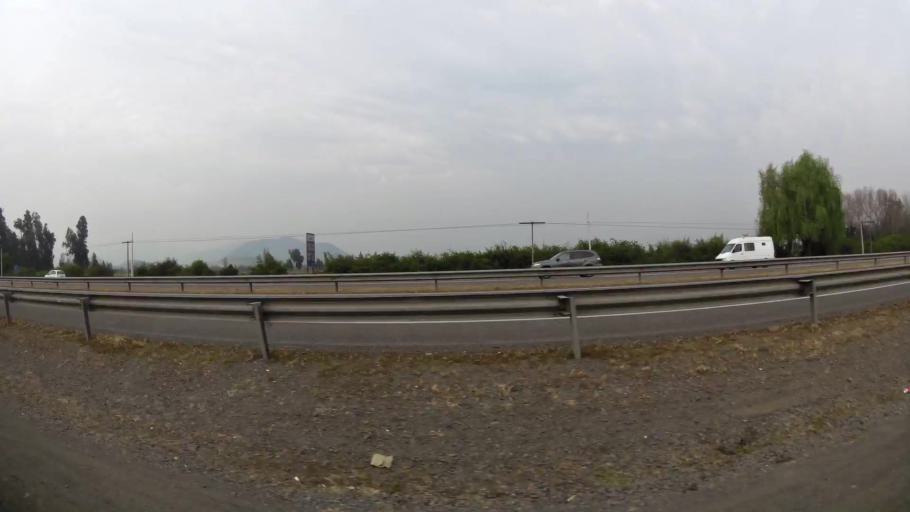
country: CL
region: Santiago Metropolitan
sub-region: Provincia de Chacabuco
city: Chicureo Abajo
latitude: -33.2655
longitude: -70.6996
